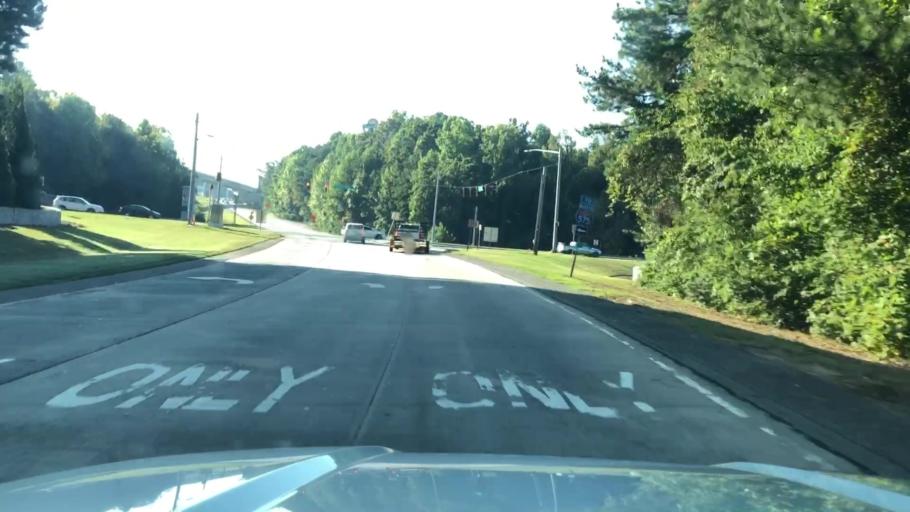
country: US
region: Georgia
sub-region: Cobb County
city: Kennesaw
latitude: 34.0099
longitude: -84.5695
